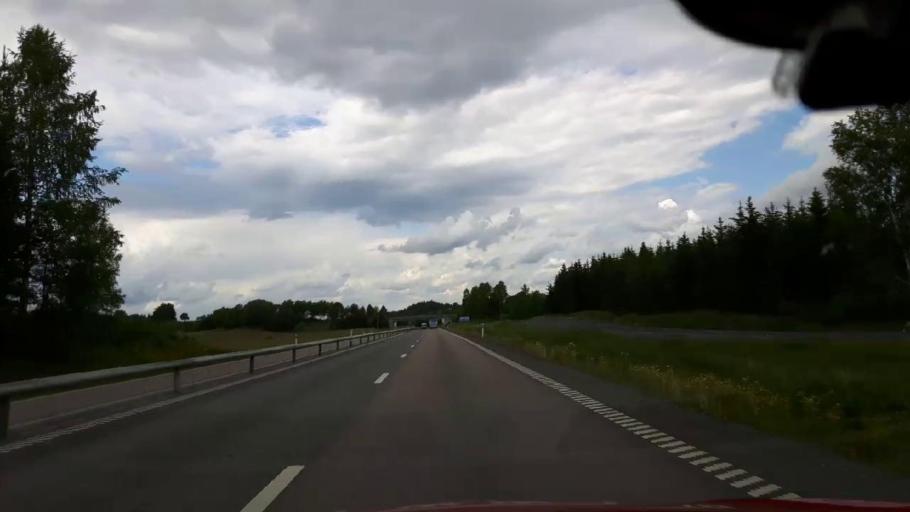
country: SE
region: Jaemtland
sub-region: Krokoms Kommun
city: Krokom
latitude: 63.3024
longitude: 14.4932
